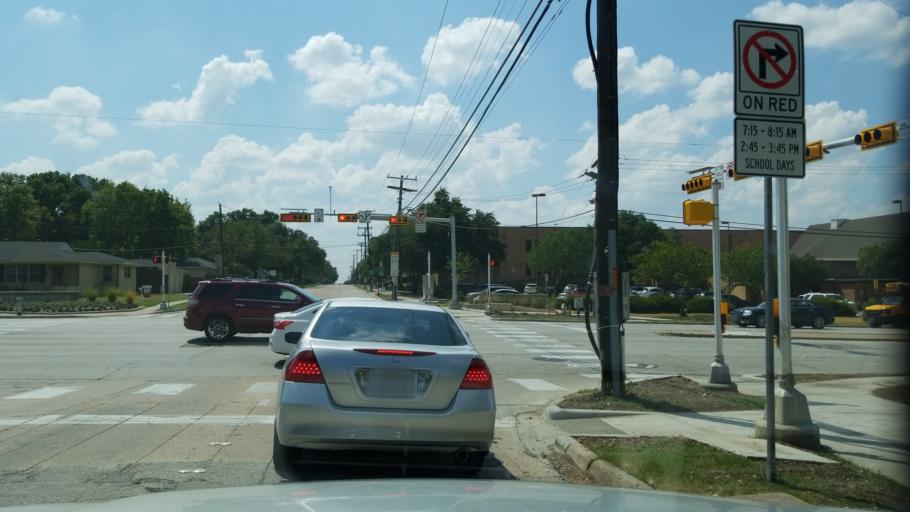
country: US
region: Texas
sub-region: Dallas County
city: Richardson
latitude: 32.9512
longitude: -96.7439
